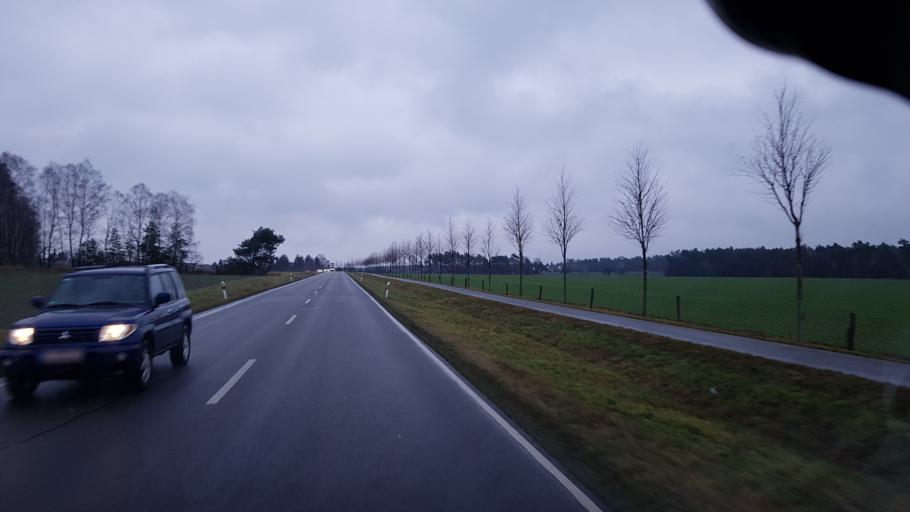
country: DE
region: Brandenburg
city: Sallgast
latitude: 51.6198
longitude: 13.7954
